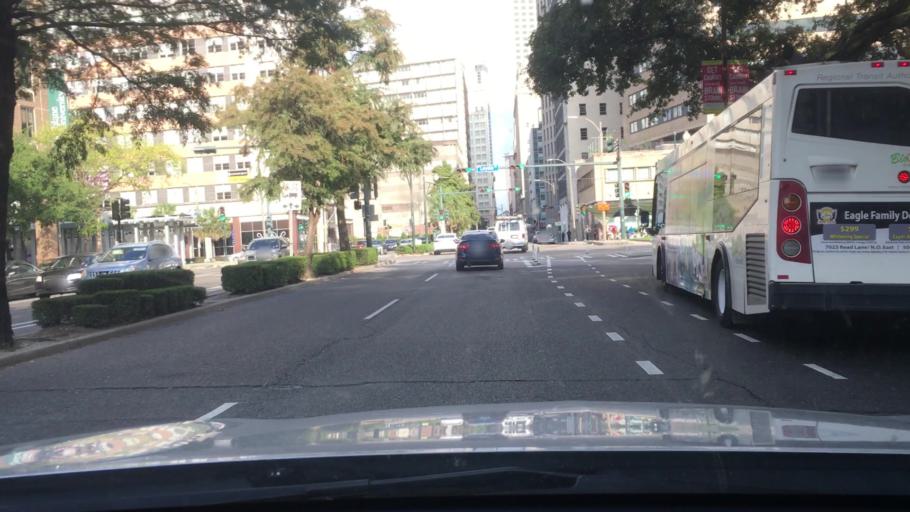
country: US
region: Louisiana
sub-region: Orleans Parish
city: New Orleans
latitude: 29.9549
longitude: -90.0754
